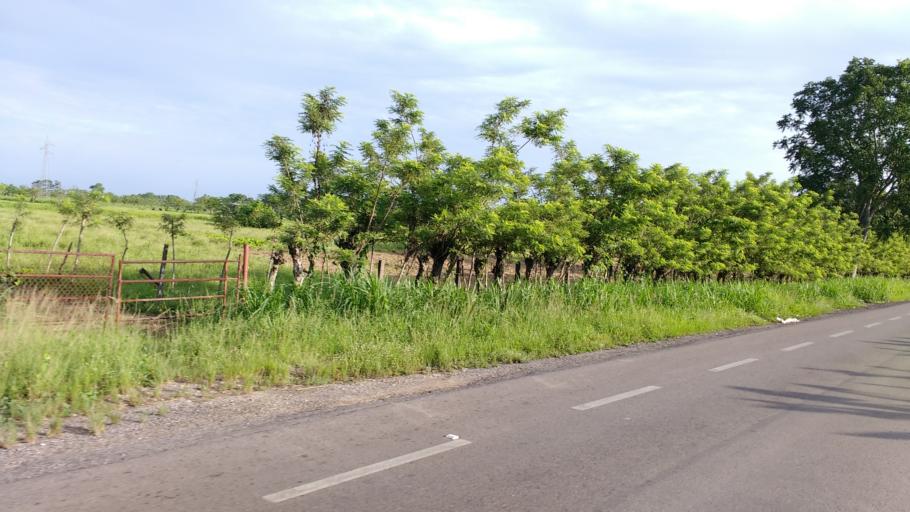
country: MX
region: Tabasco
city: Teapa
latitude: 17.5985
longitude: -92.9631
